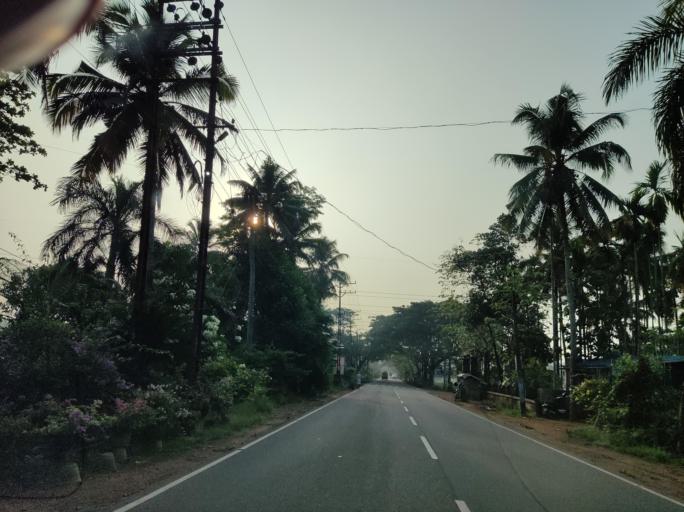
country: IN
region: Kerala
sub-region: Alappuzha
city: Kattanam
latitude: 9.1737
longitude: 76.5837
